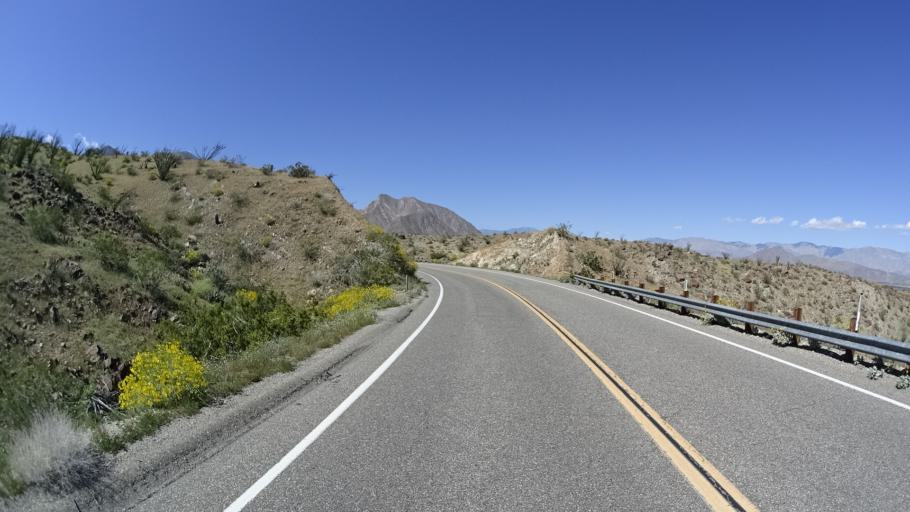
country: US
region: California
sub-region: San Diego County
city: Borrego Springs
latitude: 33.2403
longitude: -116.4033
